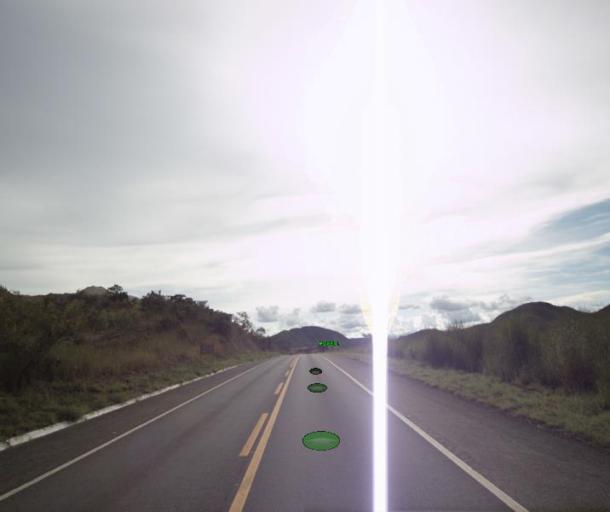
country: BR
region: Goias
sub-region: Barro Alto
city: Barro Alto
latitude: -15.1217
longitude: -48.7179
